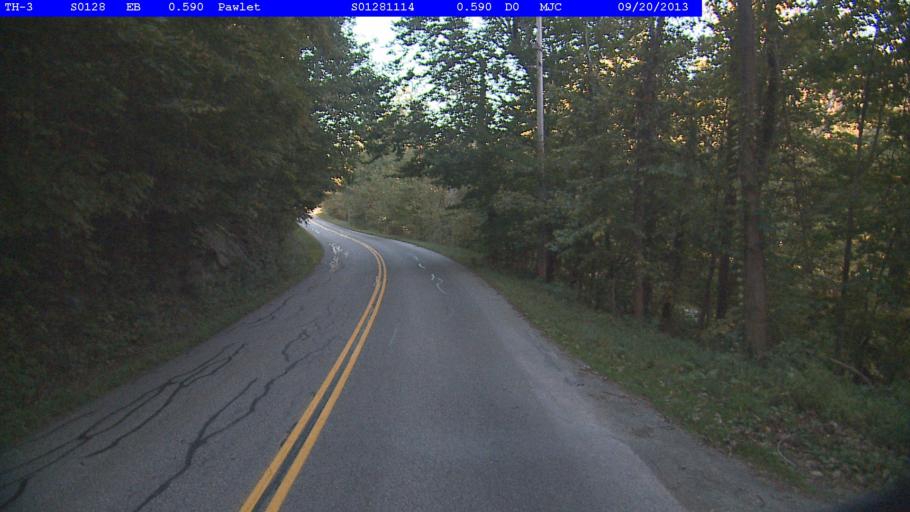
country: US
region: New York
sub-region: Washington County
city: Granville
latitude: 43.3707
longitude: -73.2189
